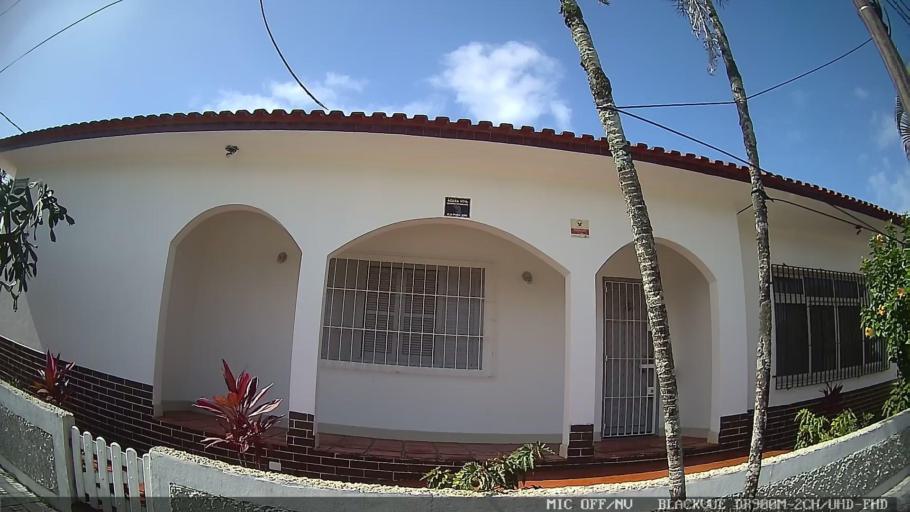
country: BR
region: Sao Paulo
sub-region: Itanhaem
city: Itanhaem
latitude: -24.1603
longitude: -46.7483
